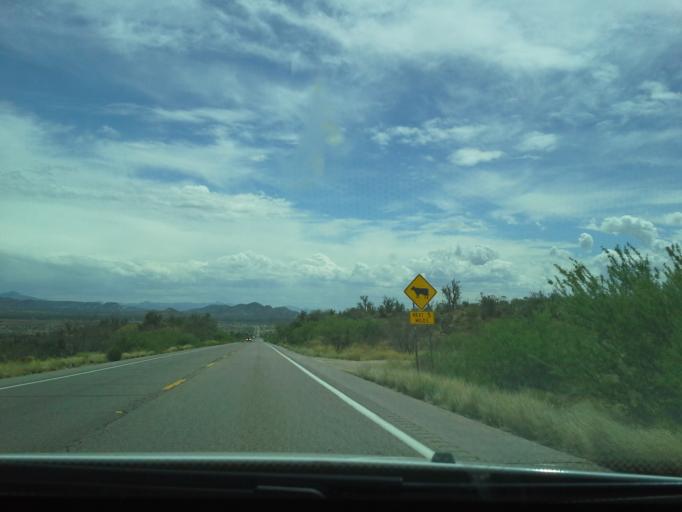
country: US
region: Arizona
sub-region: Gila County
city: Peridot
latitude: 33.3064
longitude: -110.4893
